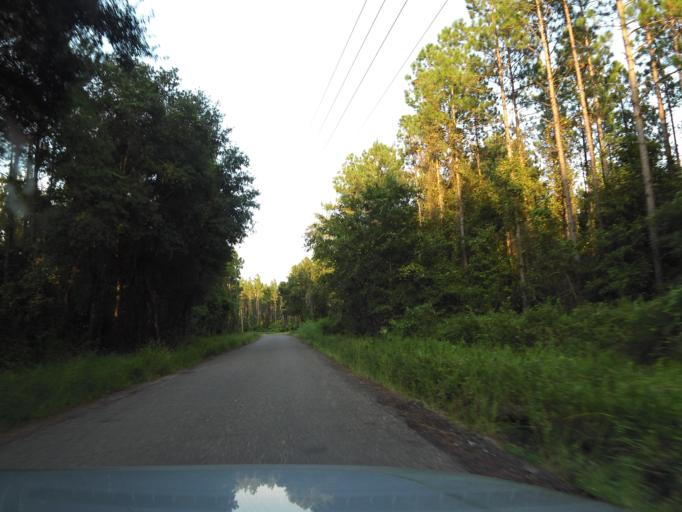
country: US
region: Florida
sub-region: Duval County
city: Baldwin
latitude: 30.3879
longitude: -82.0545
